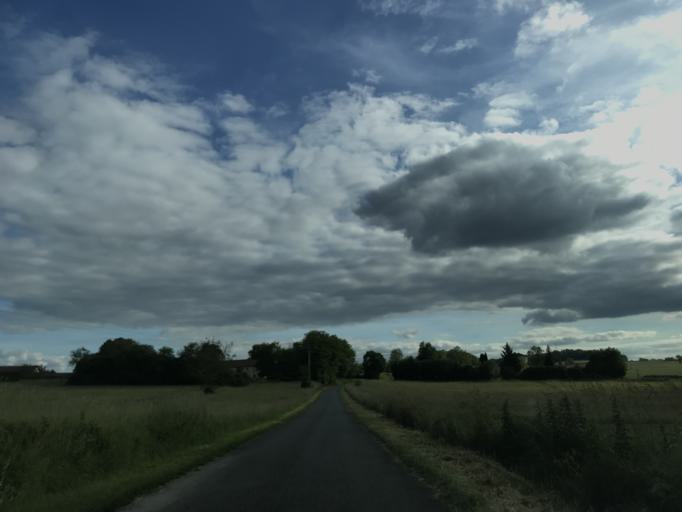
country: FR
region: Aquitaine
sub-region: Departement de la Dordogne
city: Saint-Aulaye
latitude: 45.2534
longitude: 0.1305
